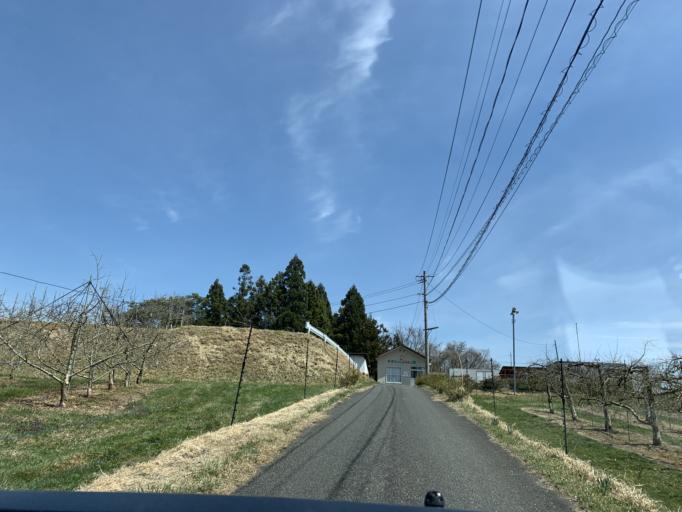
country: JP
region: Iwate
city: Ichinoseki
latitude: 38.8413
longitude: 141.2884
